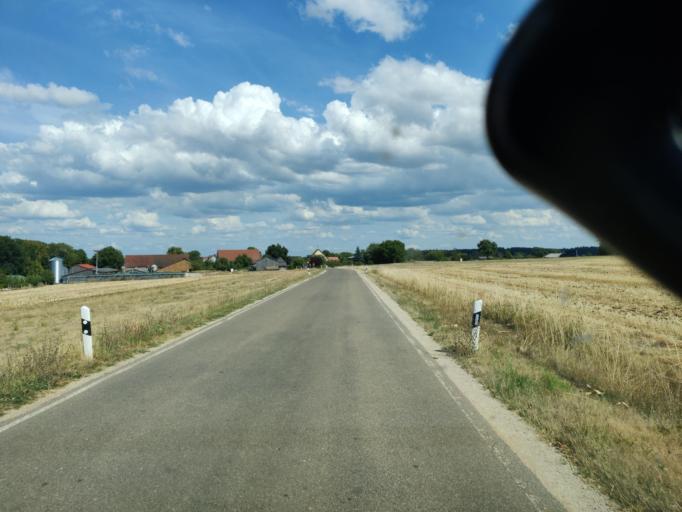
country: DE
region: Bavaria
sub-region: Regierungsbezirk Mittelfranken
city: Thalmassing
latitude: 49.0651
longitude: 11.2413
